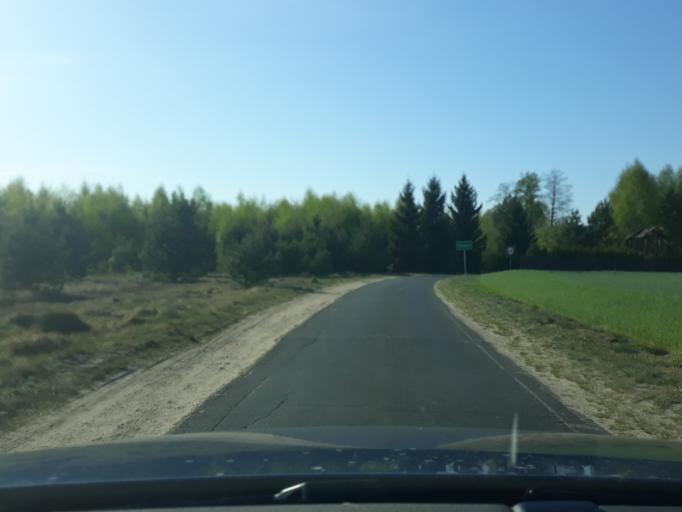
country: PL
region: Pomeranian Voivodeship
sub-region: Powiat czluchowski
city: Przechlewo
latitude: 53.8781
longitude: 17.3236
